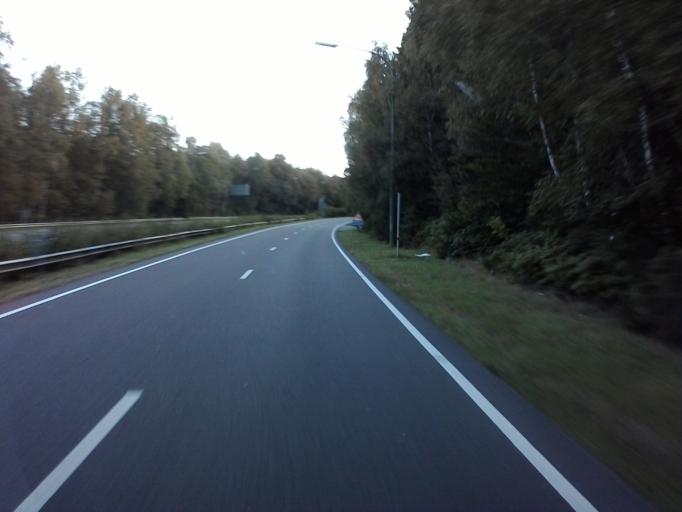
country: BE
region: Wallonia
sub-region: Province du Luxembourg
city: Tenneville
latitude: 50.1057
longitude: 5.4721
